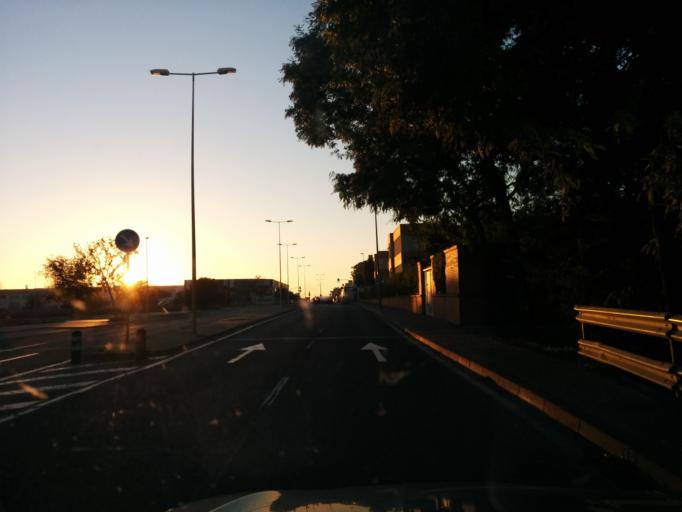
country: ES
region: Andalusia
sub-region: Provincia de Sevilla
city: Sevilla
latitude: 37.3775
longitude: -5.9336
